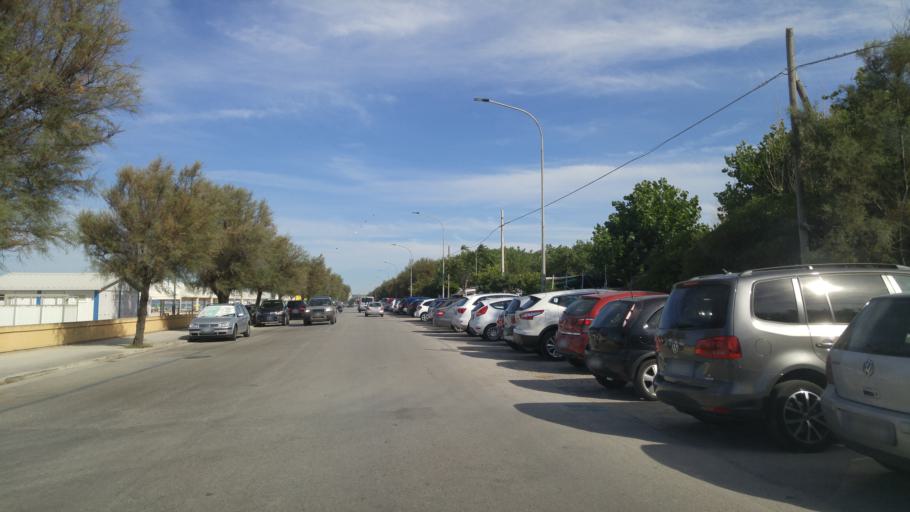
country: IT
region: The Marches
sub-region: Provincia di Ancona
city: Montignano-Marzocca
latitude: 43.6915
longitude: 13.2628
